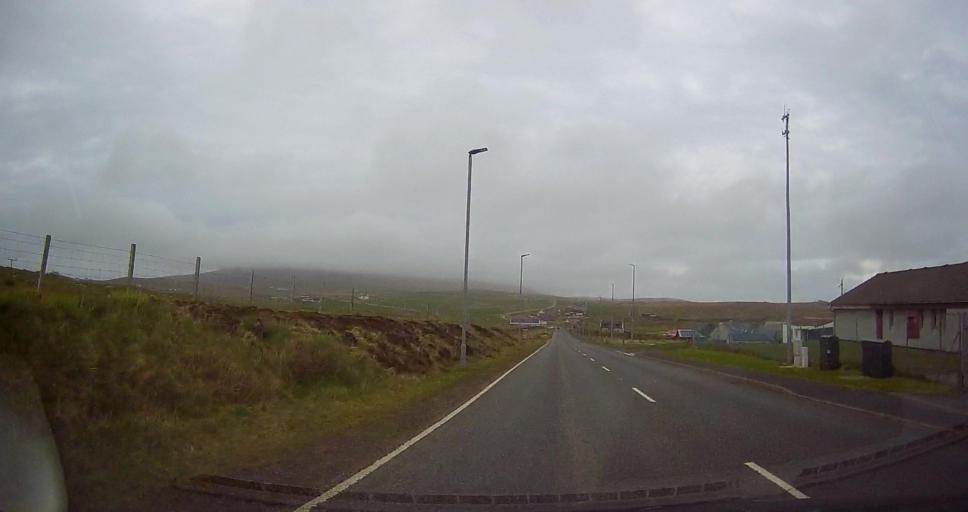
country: GB
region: Scotland
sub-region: Shetland Islands
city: Sandwick
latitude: 59.9210
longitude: -1.2994
